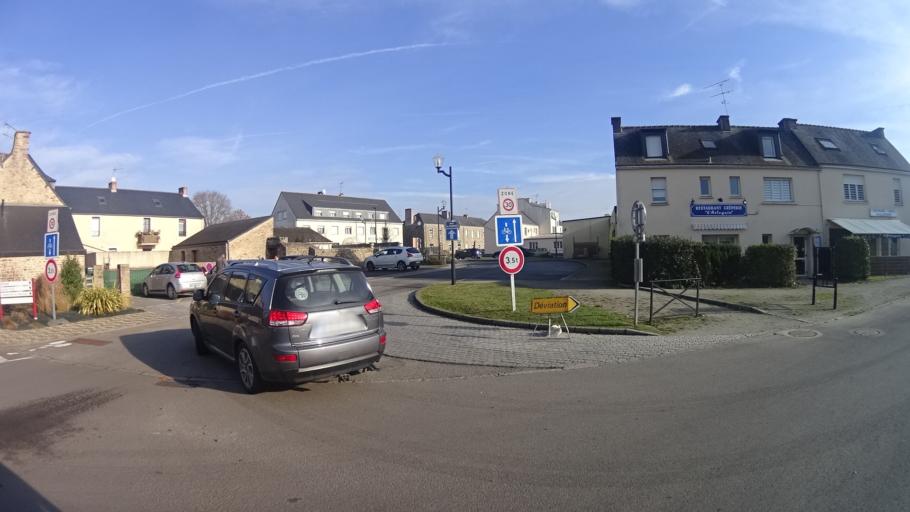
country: FR
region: Brittany
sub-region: Departement du Morbihan
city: Allaire
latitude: 47.6360
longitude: -2.1651
